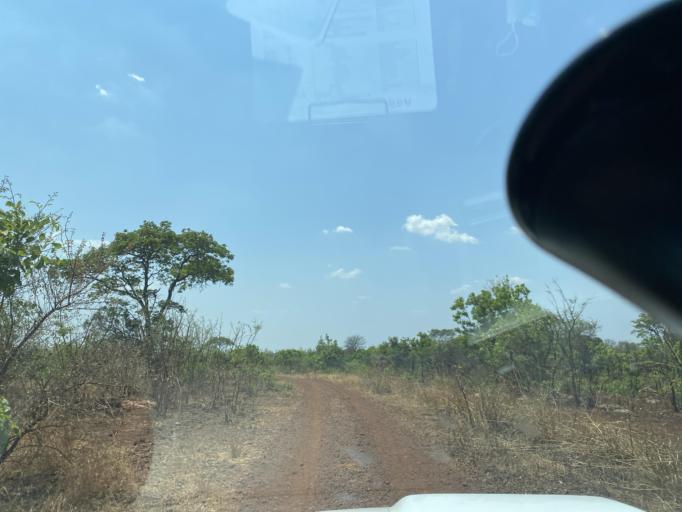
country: ZM
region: Lusaka
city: Lusaka
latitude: -15.4980
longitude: 27.9688
